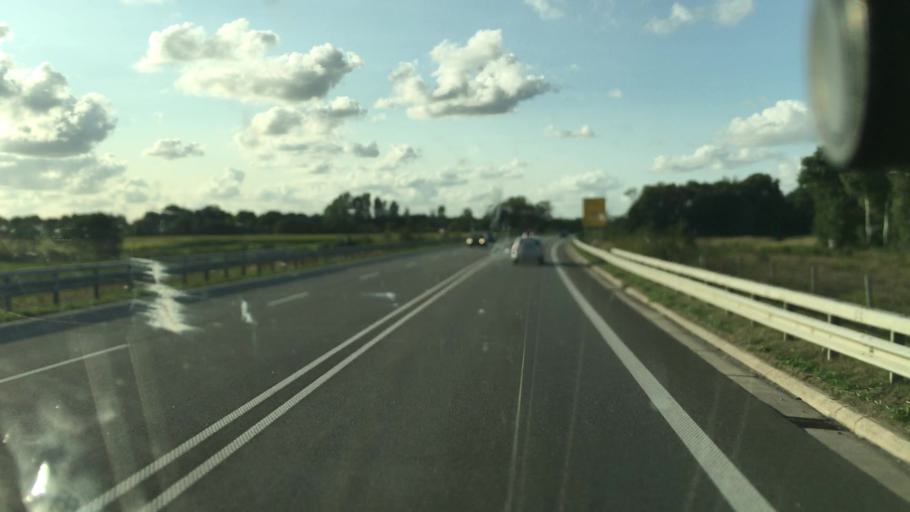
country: DE
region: Lower Saxony
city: Schortens
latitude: 53.5572
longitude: 7.9463
